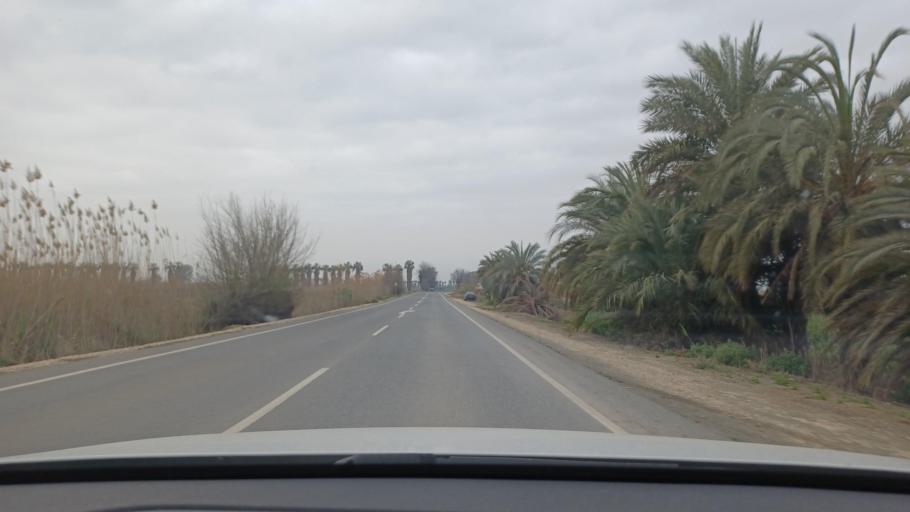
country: ES
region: Valencia
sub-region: Provincia de Alicante
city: Daya Vieja
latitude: 38.1505
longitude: -0.7164
